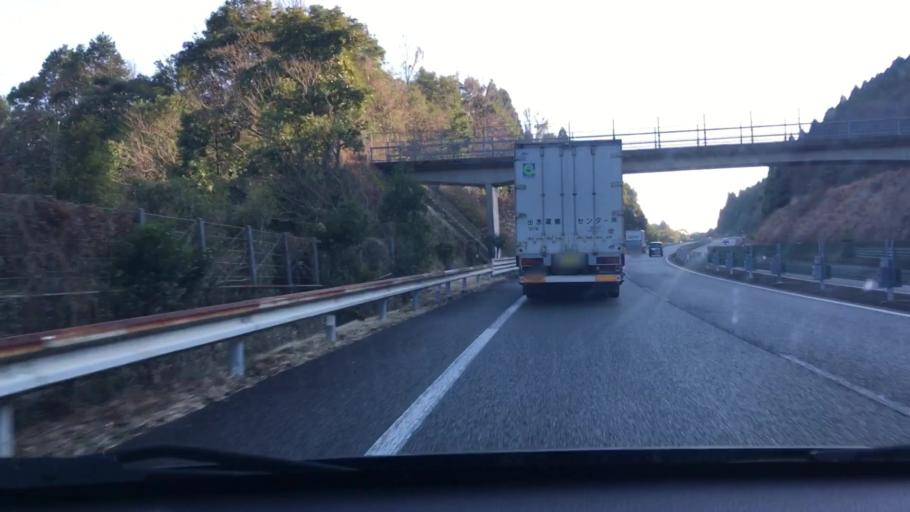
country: JP
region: Kagoshima
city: Kajiki
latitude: 31.8290
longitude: 130.6939
